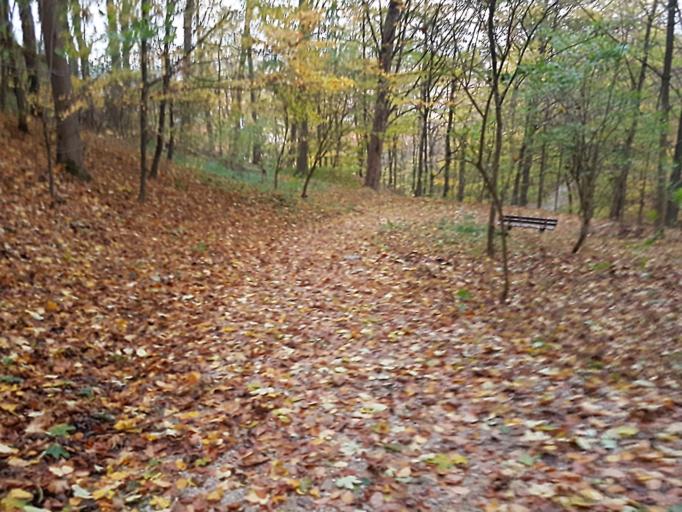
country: DE
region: Bavaria
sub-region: Lower Bavaria
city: Landshut
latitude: 48.5321
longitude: 12.1550
